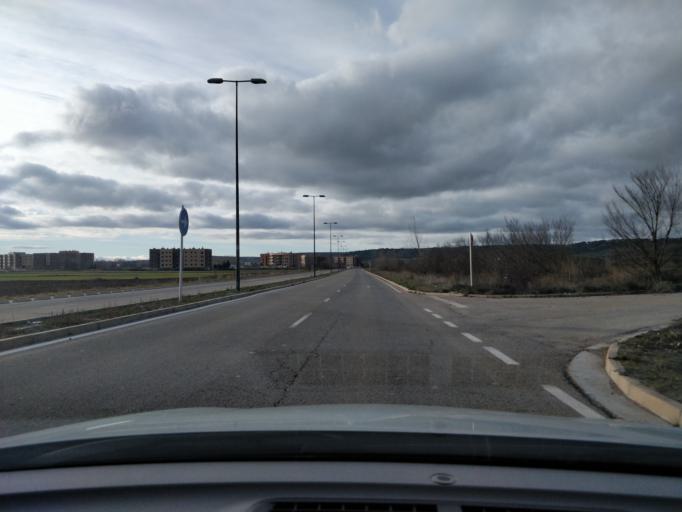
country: ES
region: Castille and Leon
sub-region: Provincia de Burgos
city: Villalbilla de Burgos
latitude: 42.3544
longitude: -3.7504
